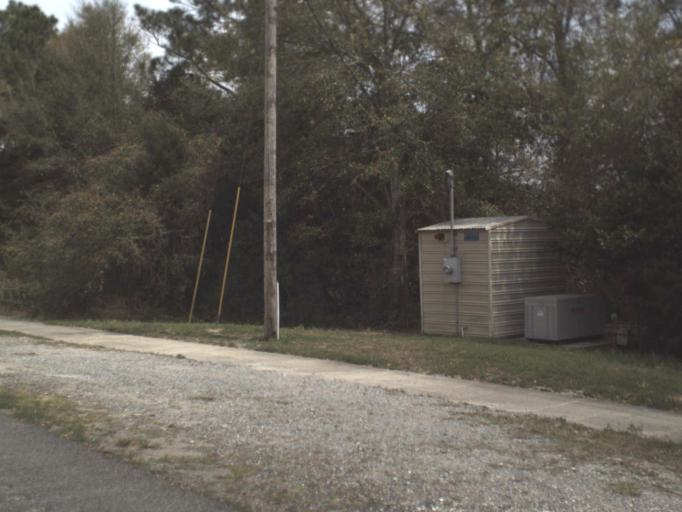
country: US
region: Florida
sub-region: Okaloosa County
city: Valparaiso
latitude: 30.5012
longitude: -86.4940
